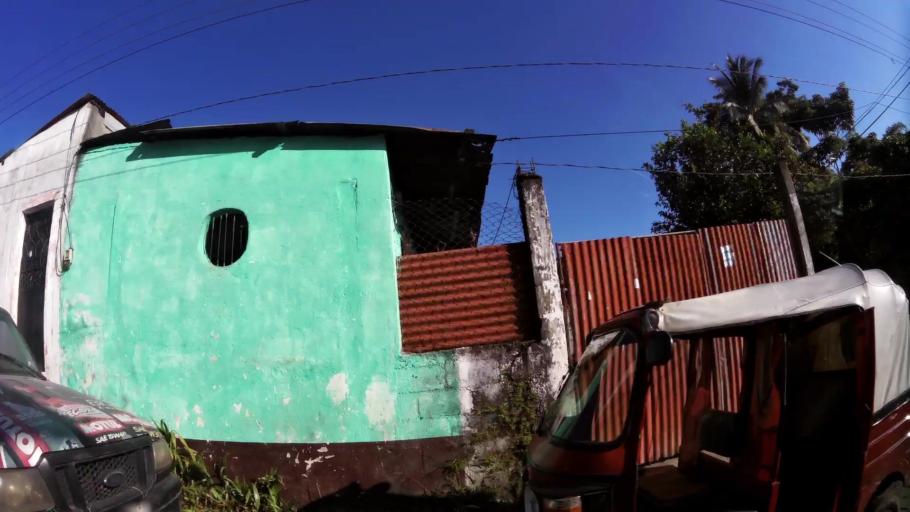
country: GT
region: Suchitepeque
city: Mazatenango
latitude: 14.5302
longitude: -91.5131
